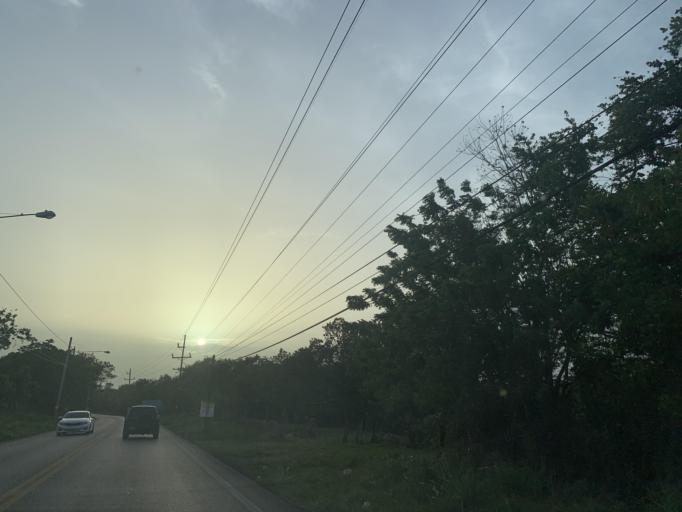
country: DO
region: Puerto Plata
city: Cabarete
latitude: 19.7781
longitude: -70.4750
